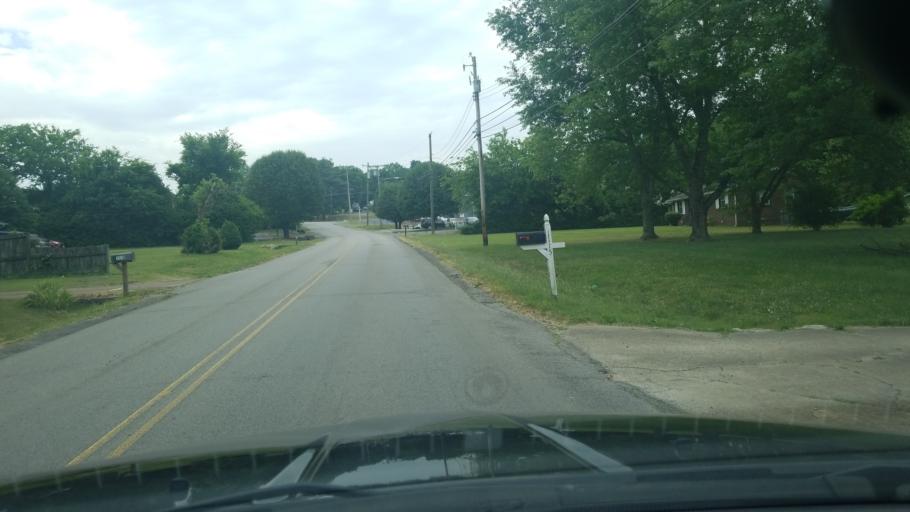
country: US
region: Tennessee
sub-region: Davidson County
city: Goodlettsville
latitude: 36.2596
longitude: -86.7601
